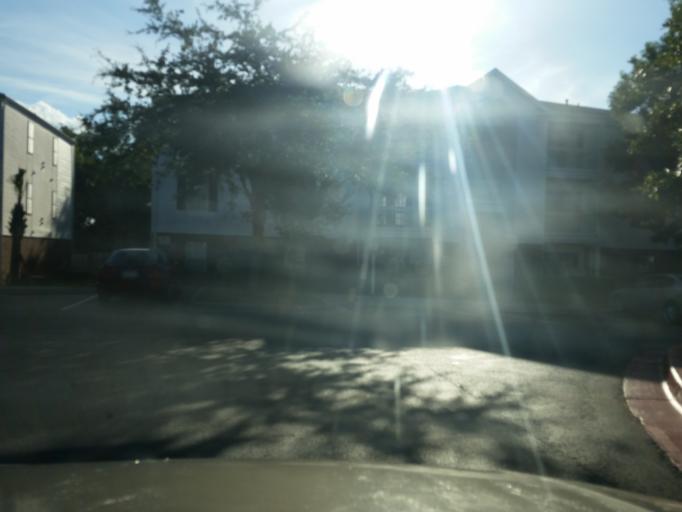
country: US
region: Florida
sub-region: Escambia County
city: Ferry Pass
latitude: 30.5276
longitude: -87.2242
